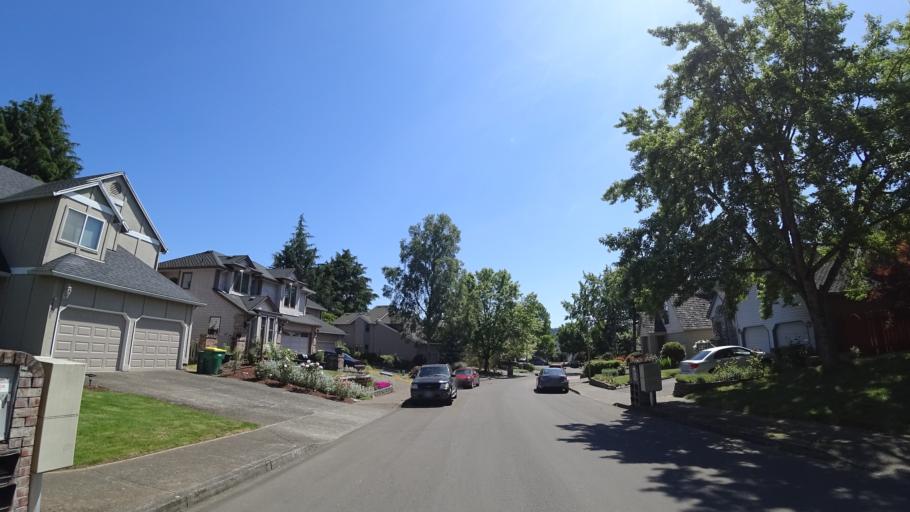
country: US
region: Oregon
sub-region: Washington County
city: Tigard
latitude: 45.4426
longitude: -122.8069
